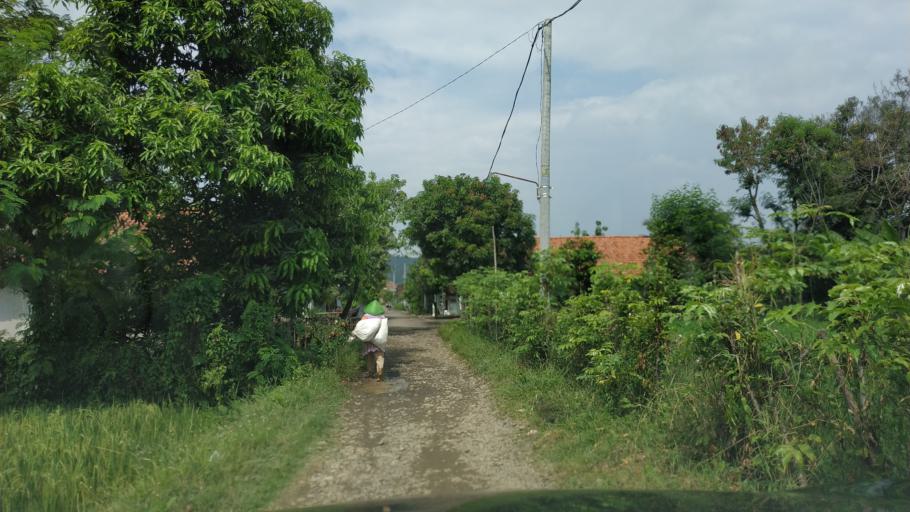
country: ID
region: Central Java
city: Margasari
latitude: -7.0927
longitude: 108.9755
